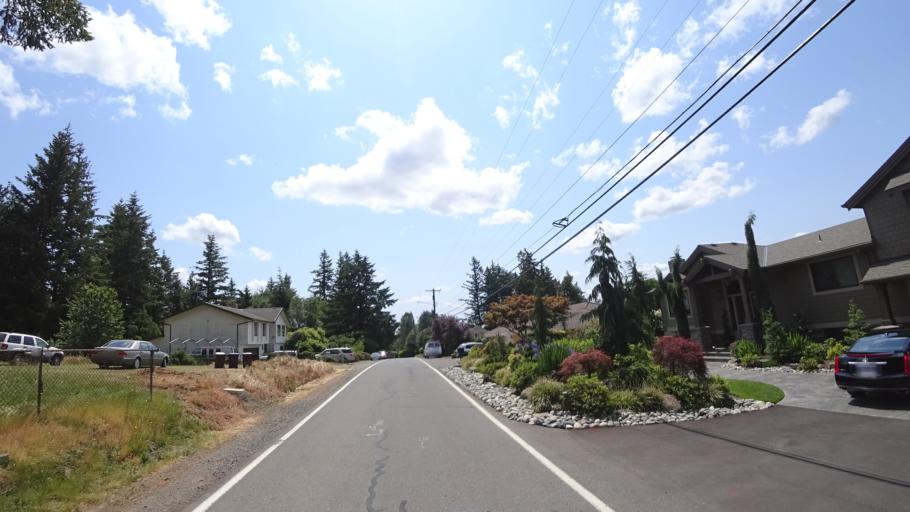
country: US
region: Oregon
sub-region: Clackamas County
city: Happy Valley
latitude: 45.4517
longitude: -122.5482
